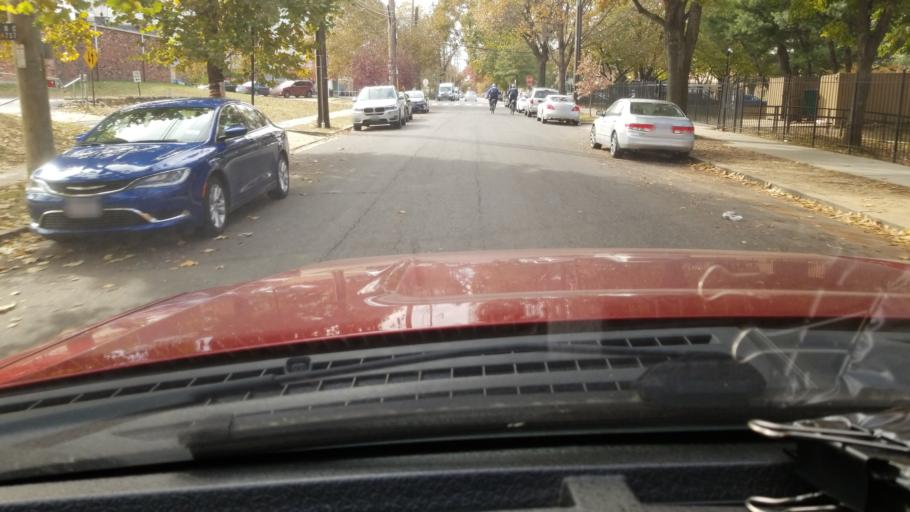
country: US
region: Maryland
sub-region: Prince George's County
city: Fairmount Heights
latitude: 38.9011
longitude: -76.9470
